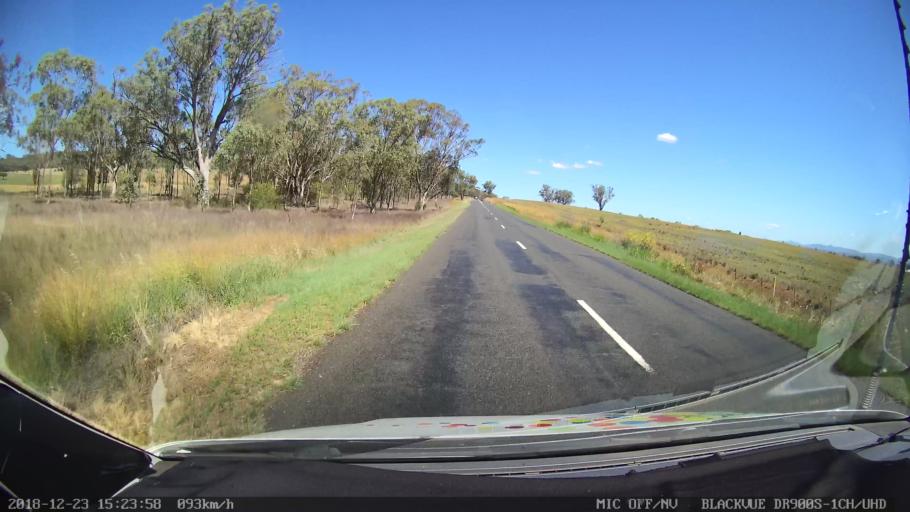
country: AU
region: New South Wales
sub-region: Tamworth Municipality
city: Manilla
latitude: -30.8863
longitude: 150.8192
